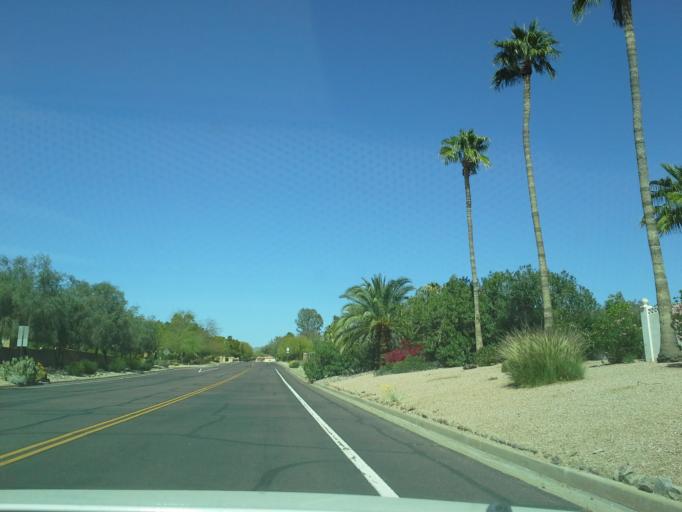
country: US
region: Arizona
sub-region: Maricopa County
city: Scottsdale
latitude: 33.5995
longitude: -111.8566
